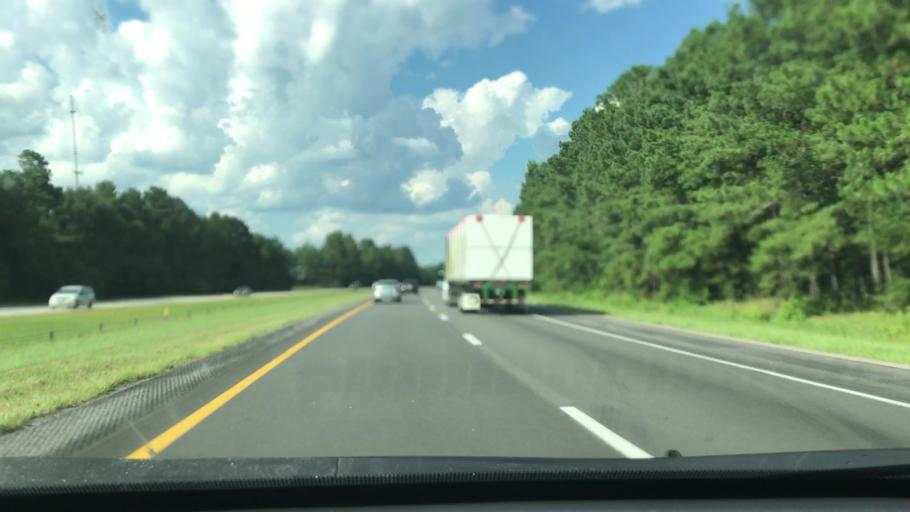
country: US
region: South Carolina
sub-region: Clarendon County
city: Manning
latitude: 33.8059
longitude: -80.1584
